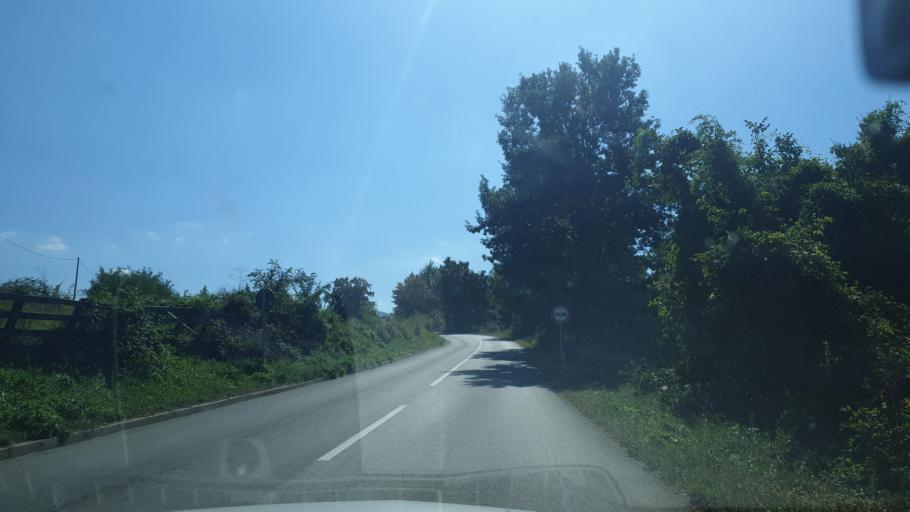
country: RS
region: Central Serbia
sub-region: Kolubarski Okrug
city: Mionica
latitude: 44.1831
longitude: 20.0332
